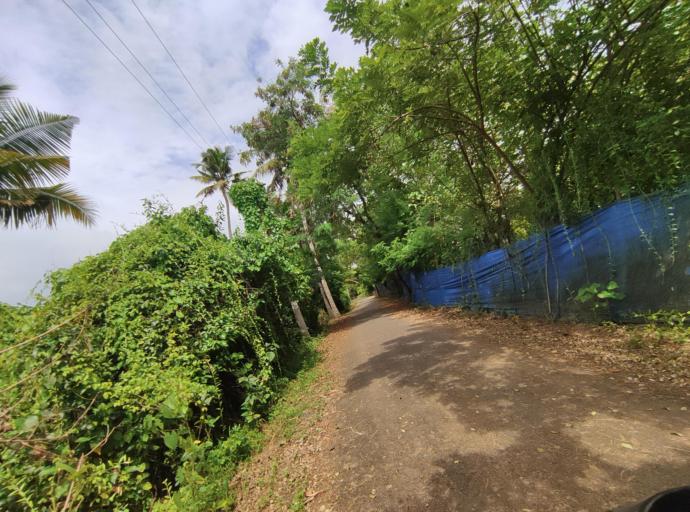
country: IN
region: Kerala
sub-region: Alappuzha
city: Kutiatodu
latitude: 9.7724
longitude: 76.2856
